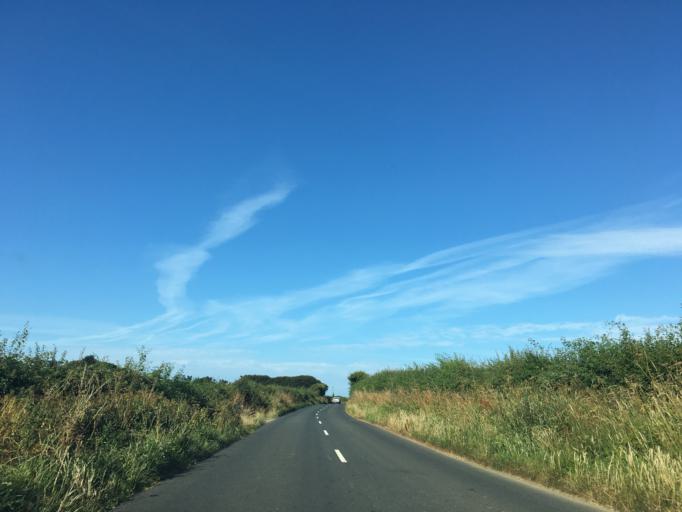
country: GB
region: England
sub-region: Isle of Wight
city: Chale
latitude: 50.6210
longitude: -1.2987
